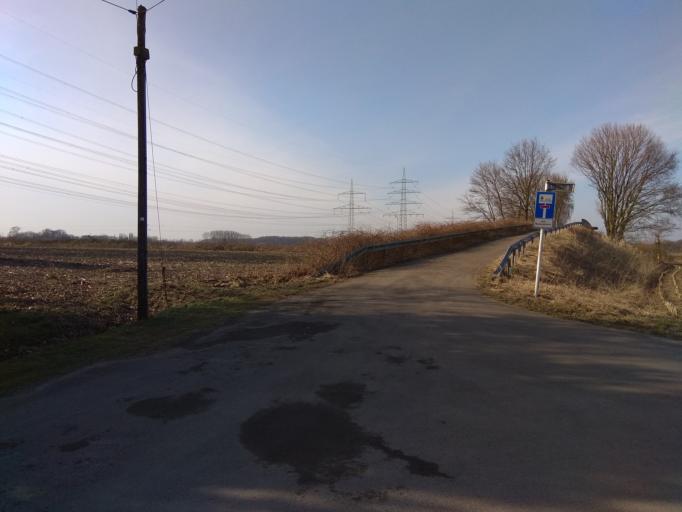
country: DE
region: North Rhine-Westphalia
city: Marl
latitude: 51.6289
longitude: 7.0763
